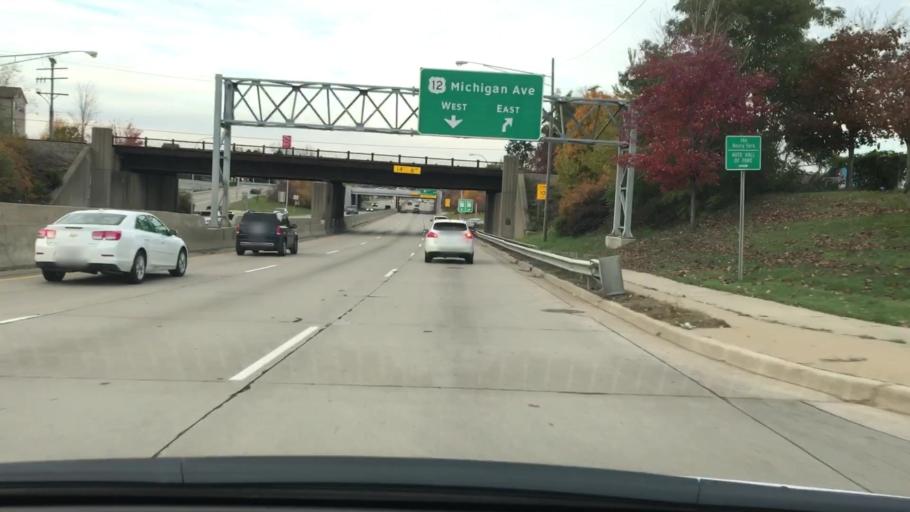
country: US
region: Michigan
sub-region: Wayne County
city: Inkster
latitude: 42.2971
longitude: -83.2712
